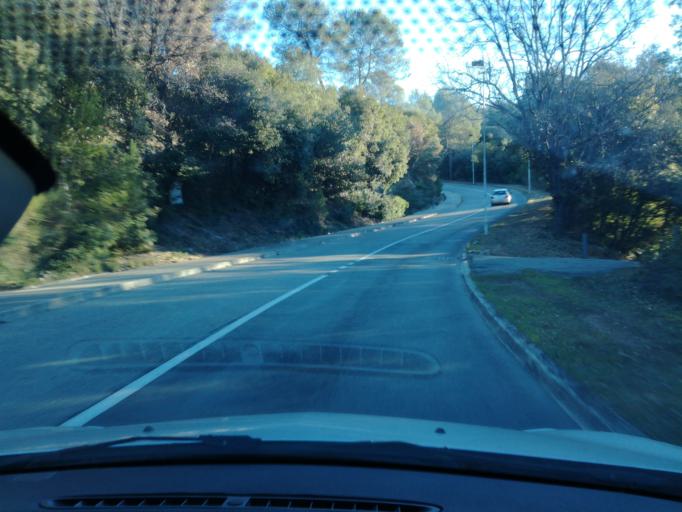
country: FR
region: Provence-Alpes-Cote d'Azur
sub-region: Departement des Alpes-Maritimes
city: Biot
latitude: 43.6156
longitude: 7.0634
